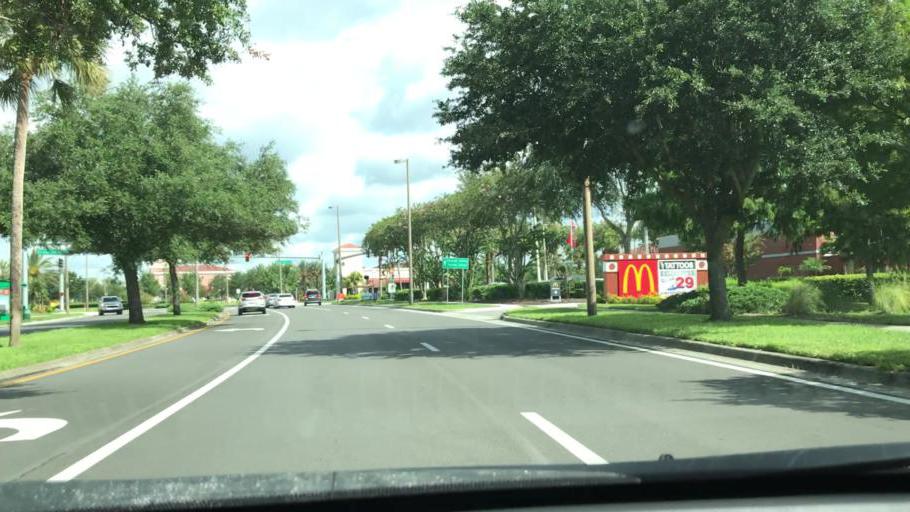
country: US
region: Florida
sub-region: Orange County
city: Williamsburg
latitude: 28.3882
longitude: -81.4888
